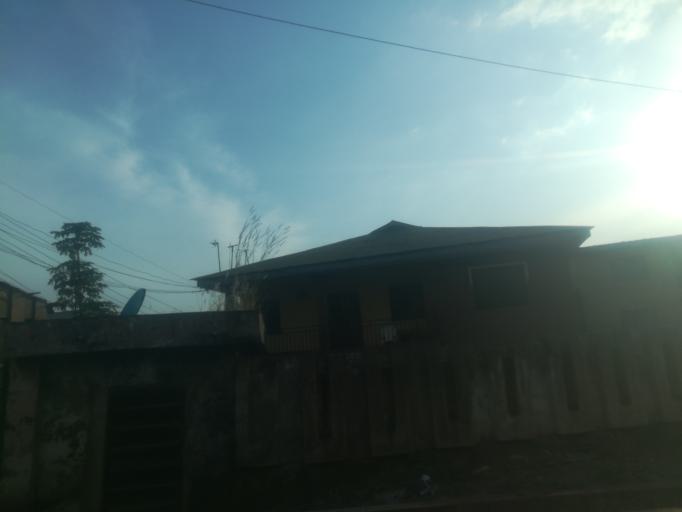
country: NG
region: Ogun
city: Abeokuta
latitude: 7.1245
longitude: 3.3226
